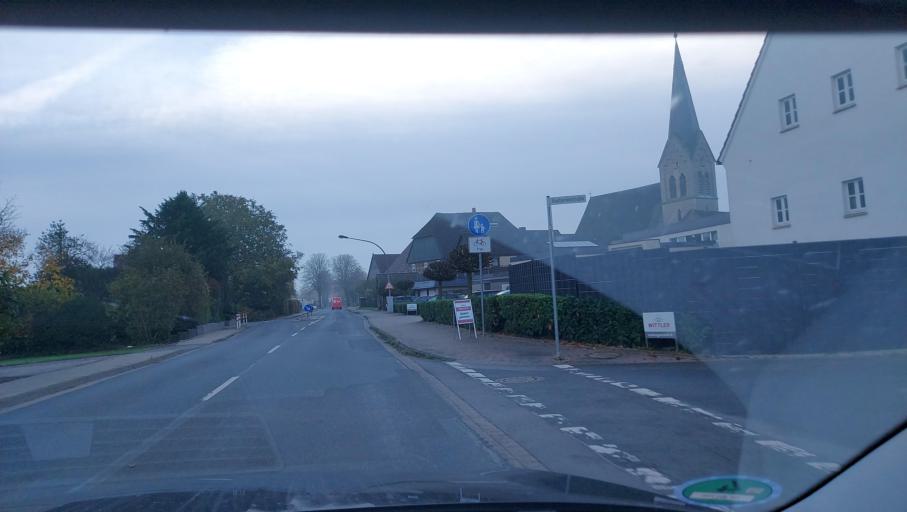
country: DE
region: Lower Saxony
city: Neuenkirchen
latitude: 52.1518
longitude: 8.4271
